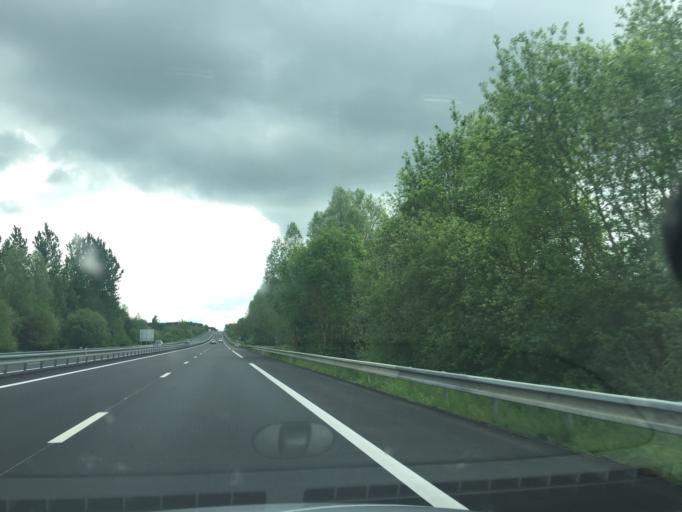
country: FR
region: Pays de la Loire
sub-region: Departement de la Sarthe
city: Champagne
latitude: 47.9757
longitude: 0.3302
